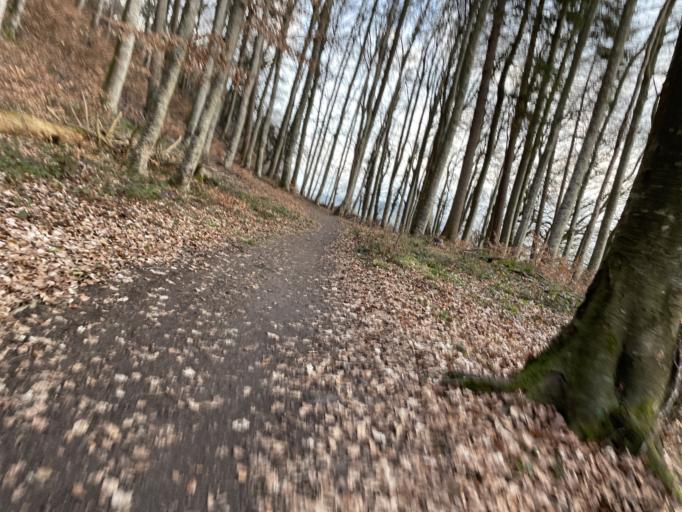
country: CH
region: Bern
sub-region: Bern-Mittelland District
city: Muhlethurnen
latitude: 46.8393
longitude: 7.5275
